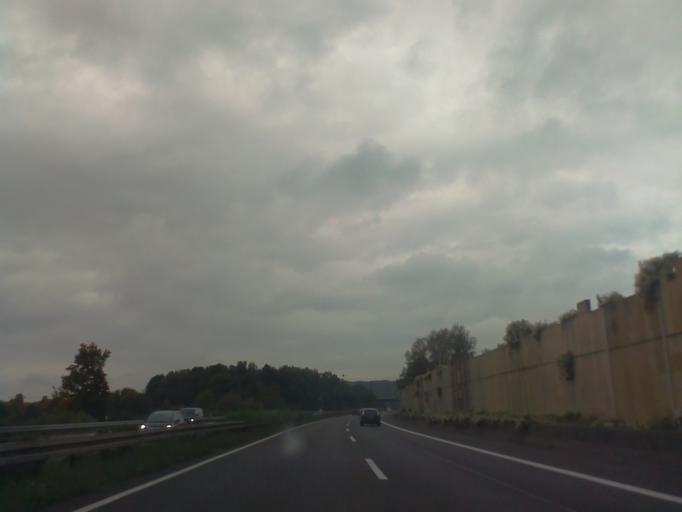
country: DE
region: Hesse
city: Hain-Grundau
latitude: 50.1932
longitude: 9.1163
